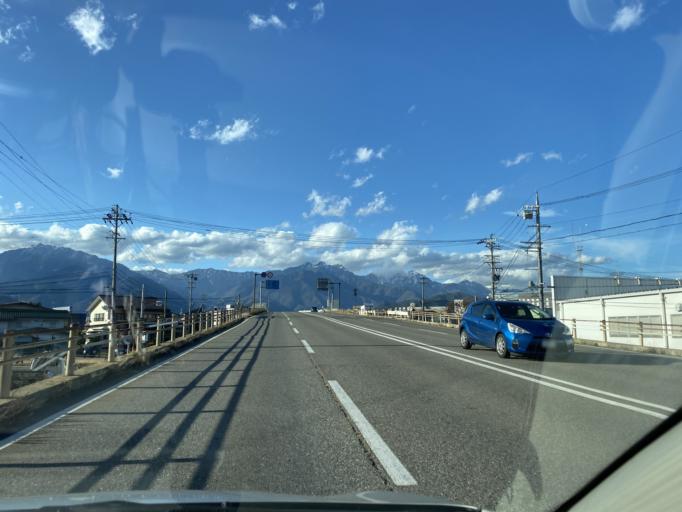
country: JP
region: Nagano
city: Omachi
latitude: 36.4968
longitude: 137.8616
